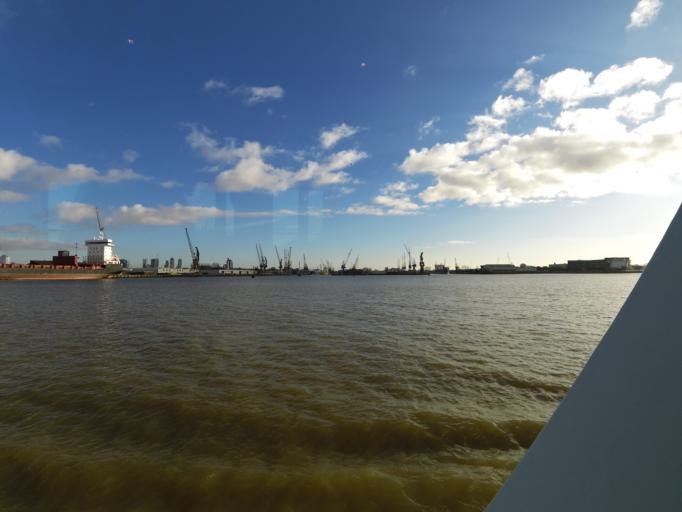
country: NL
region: South Holland
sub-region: Gemeente Rotterdam
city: Delfshaven
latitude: 51.8948
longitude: 4.4380
